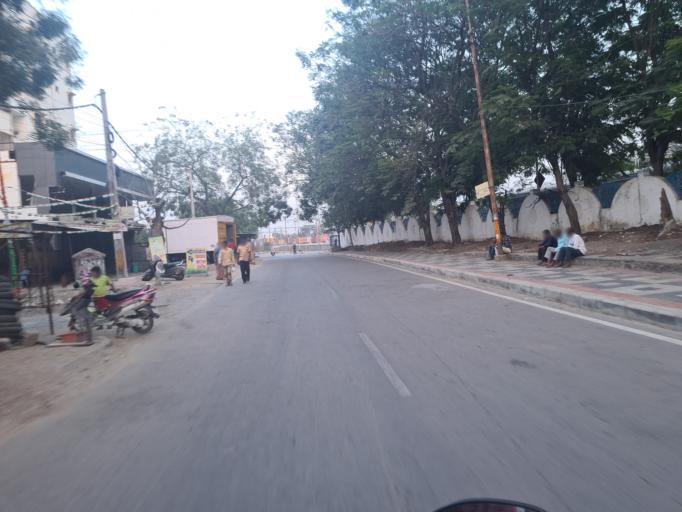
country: IN
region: Telangana
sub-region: Medak
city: Serilingampalle
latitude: 17.4838
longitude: 78.3174
